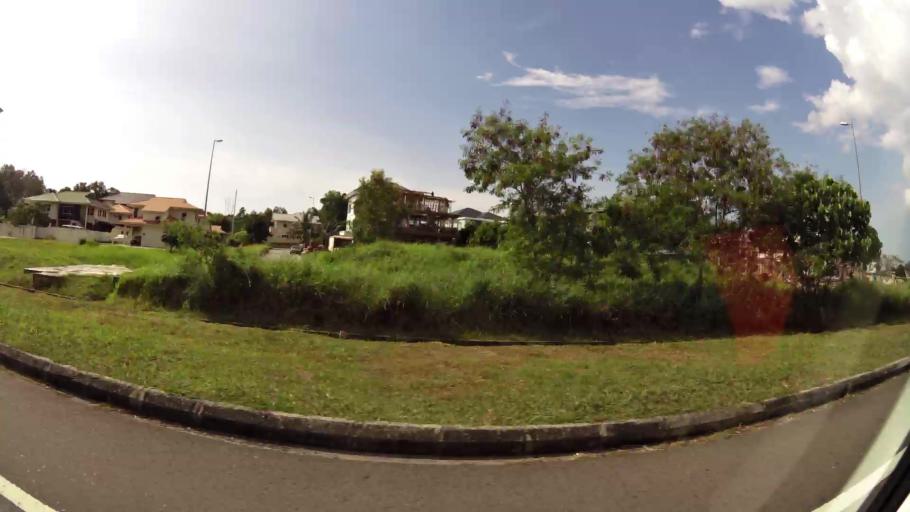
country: BN
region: Brunei and Muara
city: Bandar Seri Begawan
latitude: 4.9517
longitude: 114.9508
